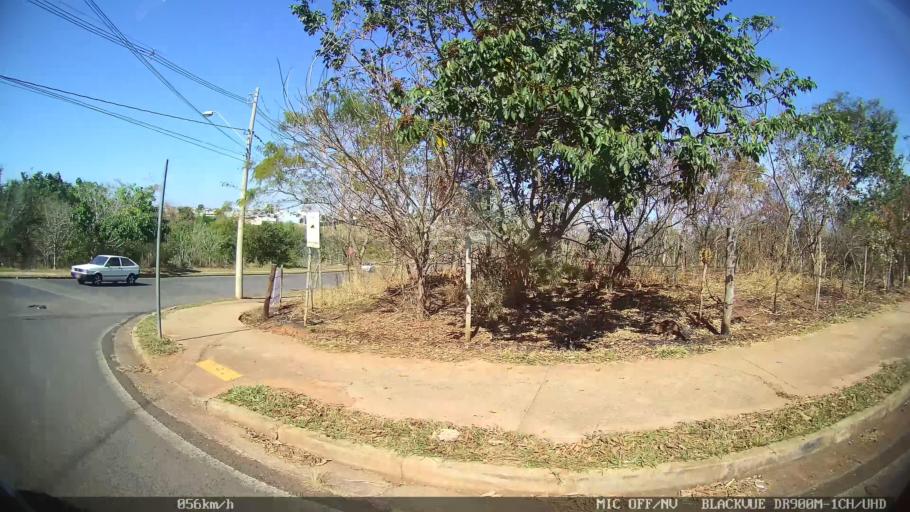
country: BR
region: Sao Paulo
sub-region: Sao Jose Do Rio Preto
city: Sao Jose do Rio Preto
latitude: -20.7602
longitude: -49.4205
